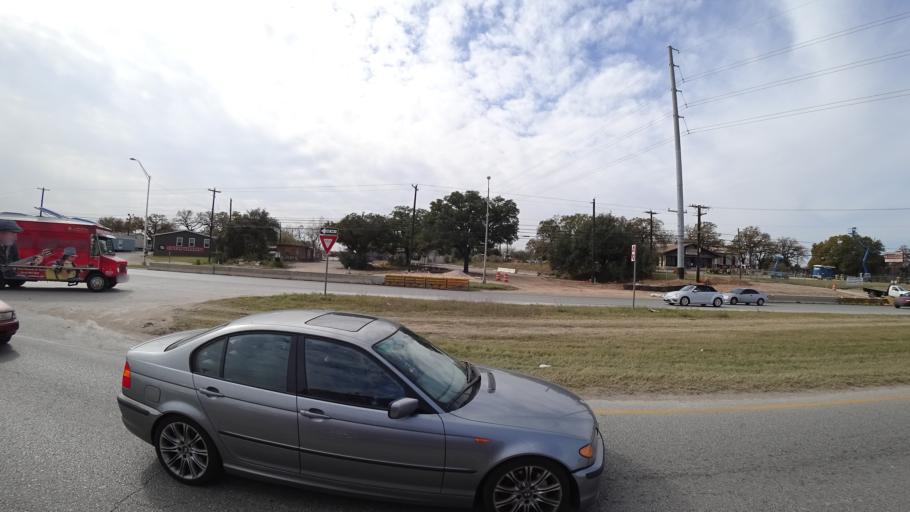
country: US
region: Texas
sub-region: Travis County
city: Austin
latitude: 30.2329
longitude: -97.6840
